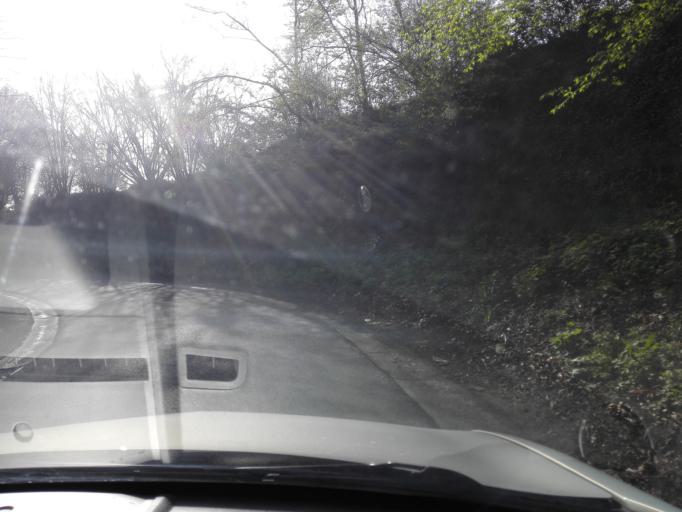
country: BE
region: Flanders
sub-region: Provincie Vlaams-Brabant
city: Aarschot
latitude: 50.9660
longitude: 4.8578
